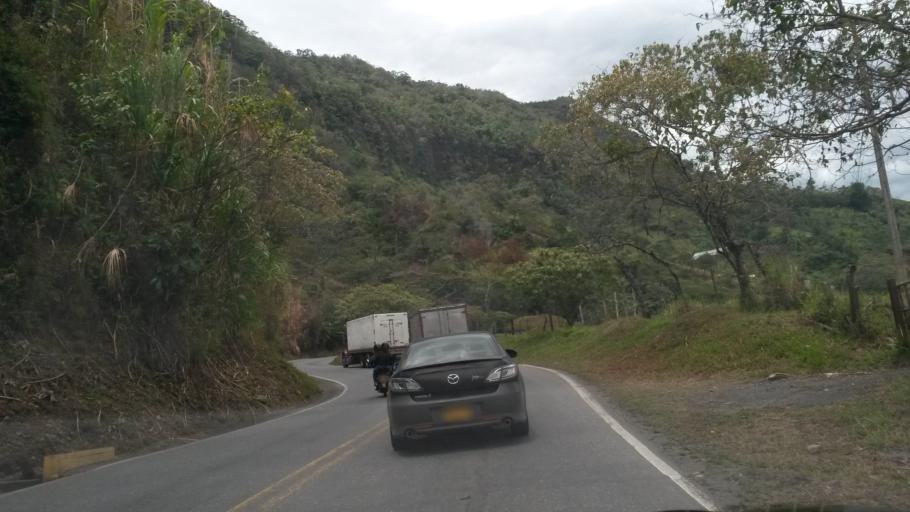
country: CO
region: Cauca
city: Rosas
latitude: 2.2582
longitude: -76.7555
